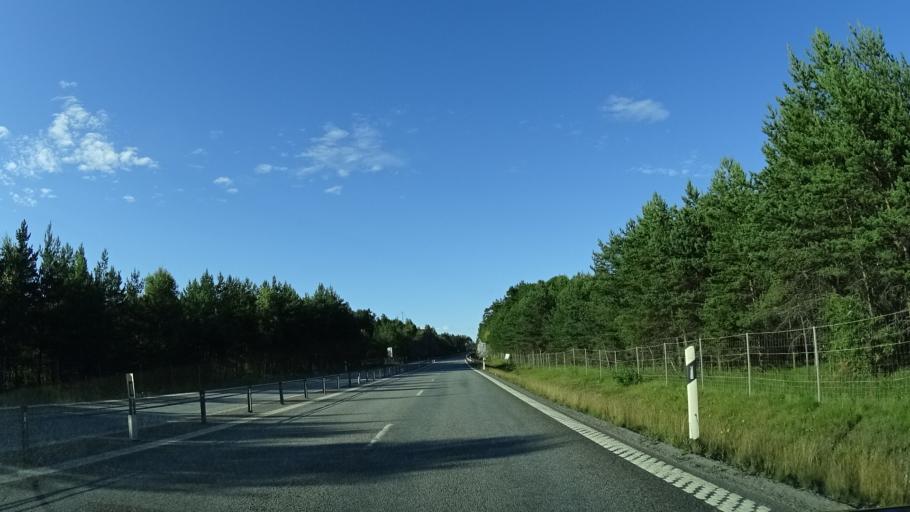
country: SE
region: Stockholm
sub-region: Osterakers Kommun
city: Akersberga
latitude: 59.5735
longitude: 18.2376
